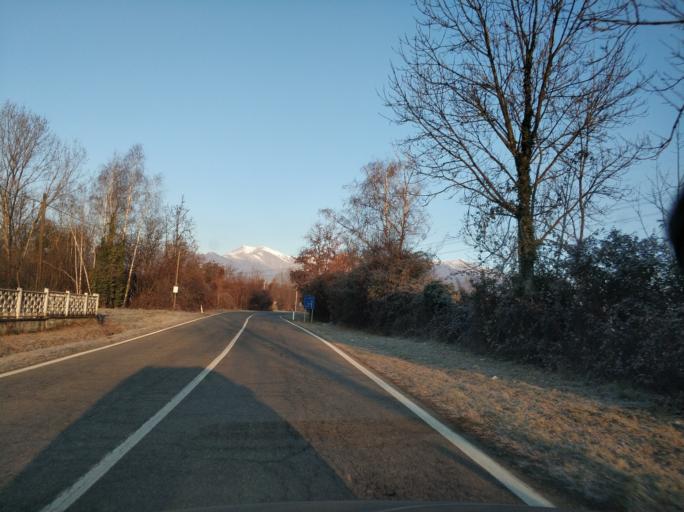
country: IT
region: Piedmont
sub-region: Provincia di Torino
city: Nole
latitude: 45.2632
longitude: 7.5814
